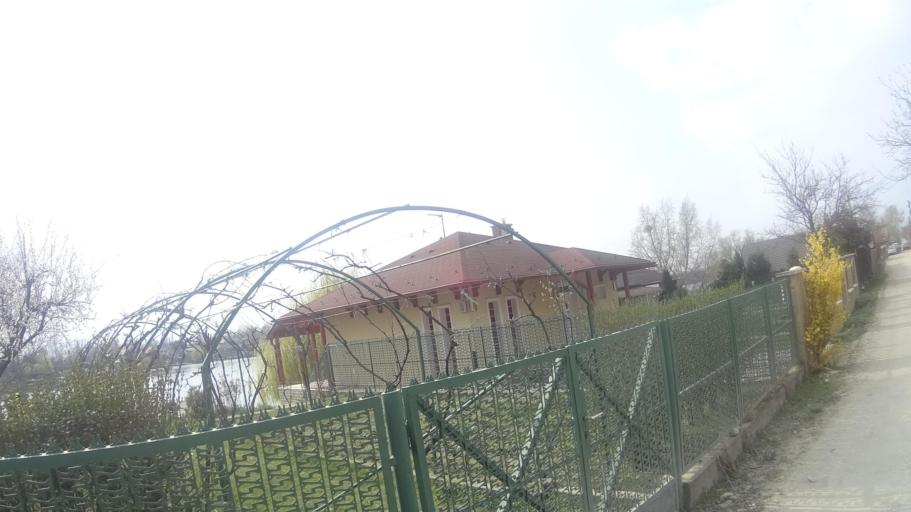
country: HU
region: Pest
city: Dunaharaszti
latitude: 47.3866
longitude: 19.0712
